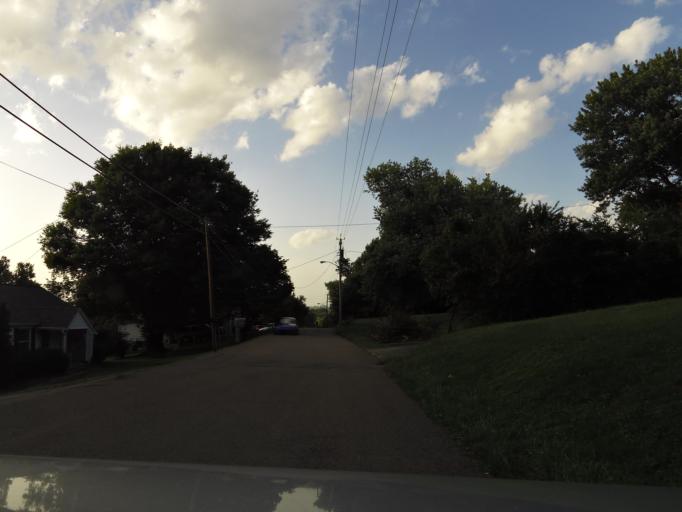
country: US
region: Tennessee
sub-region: Knox County
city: Knoxville
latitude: 35.9457
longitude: -83.8820
